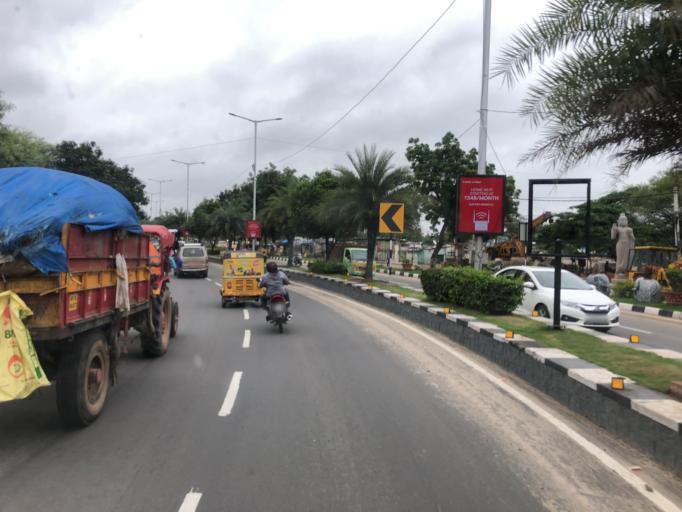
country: IN
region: Telangana
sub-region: Rangareddi
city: Kukatpalli
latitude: 17.4585
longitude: 78.3773
